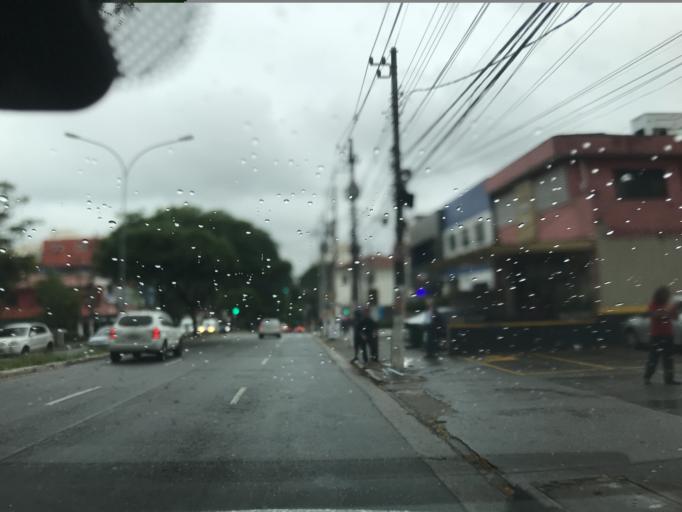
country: BR
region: Sao Paulo
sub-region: Sao Paulo
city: Sao Paulo
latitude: -23.5307
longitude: -46.6853
